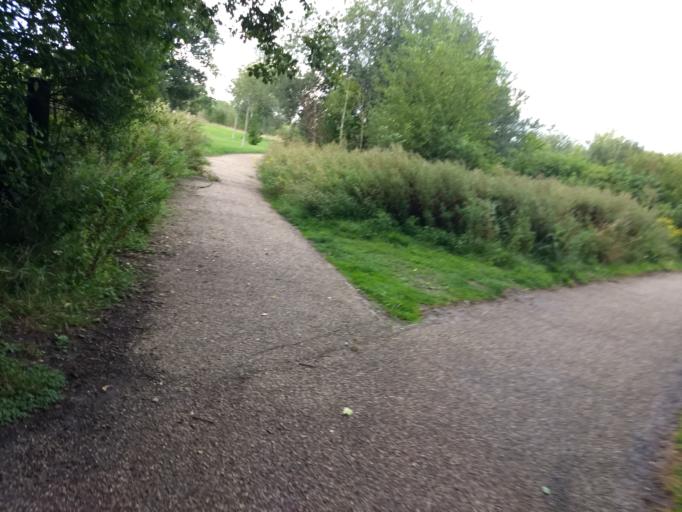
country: GB
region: England
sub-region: Buckinghamshire
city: Newton Longville
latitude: 51.9878
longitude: -0.8013
